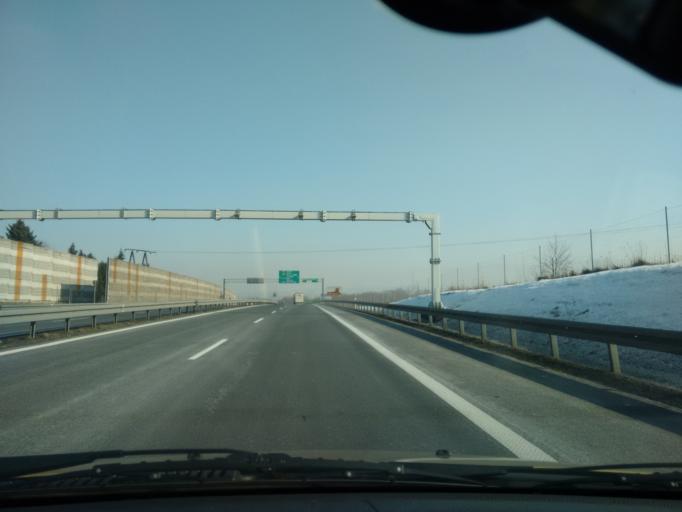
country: PL
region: Silesian Voivodeship
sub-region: Bielsko-Biala
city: Bielsko-Biala
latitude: 49.8473
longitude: 19.0212
